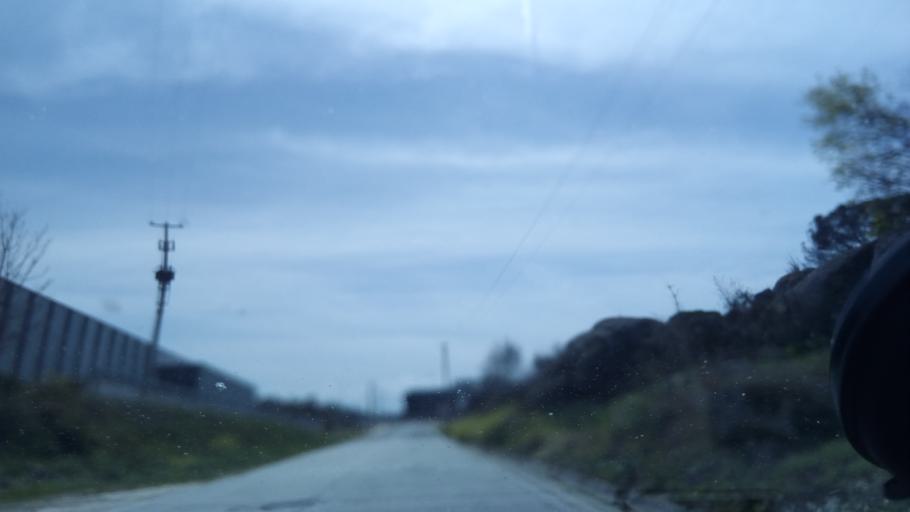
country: PT
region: Viseu
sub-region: Mangualde
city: Mangualde
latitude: 40.6108
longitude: -7.7886
